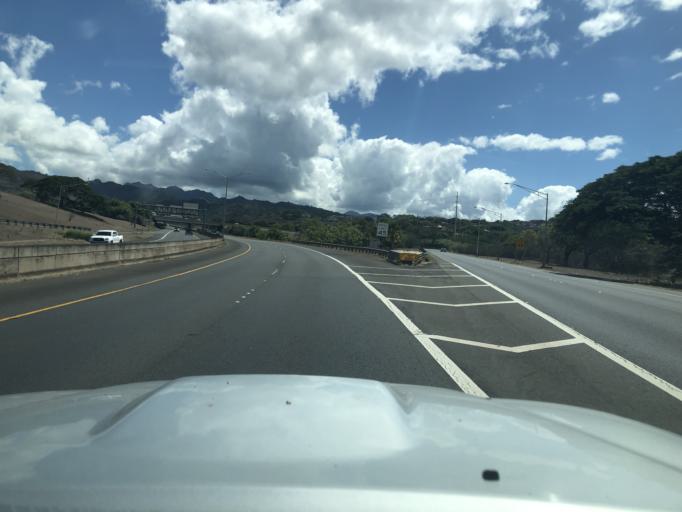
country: US
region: Hawaii
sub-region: Honolulu County
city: Halawa Heights
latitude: 21.3696
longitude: -157.9187
